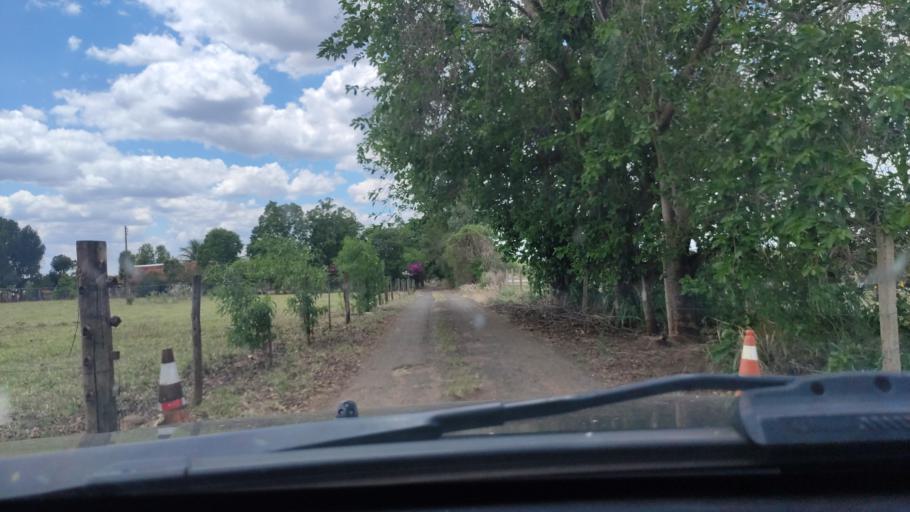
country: BR
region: Sao Paulo
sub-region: Duartina
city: Duartina
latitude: -22.6510
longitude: -49.4073
